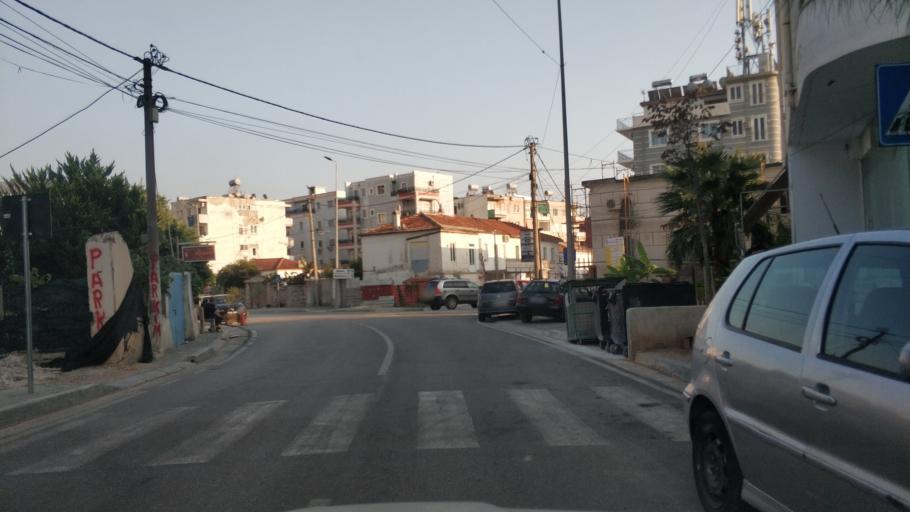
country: AL
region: Vlore
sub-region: Rrethi i Vlores
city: Himare
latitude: 40.1031
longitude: 19.7436
